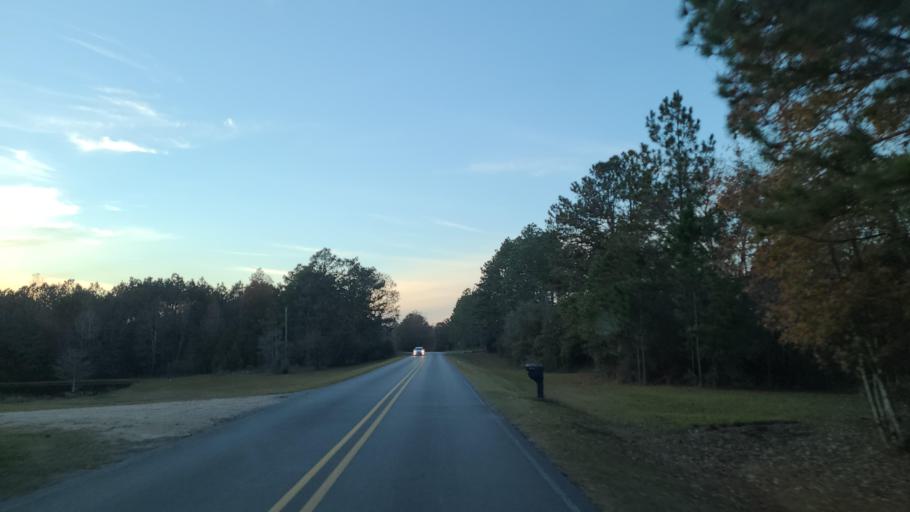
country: US
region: Mississippi
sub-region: Perry County
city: New Augusta
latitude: 31.0726
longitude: -89.2035
